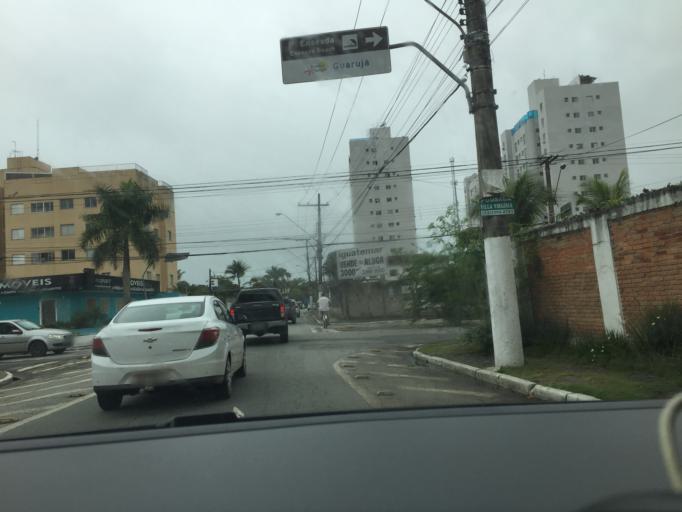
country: BR
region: Sao Paulo
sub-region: Guaruja
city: Guaruja
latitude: -23.9792
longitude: -46.2224
